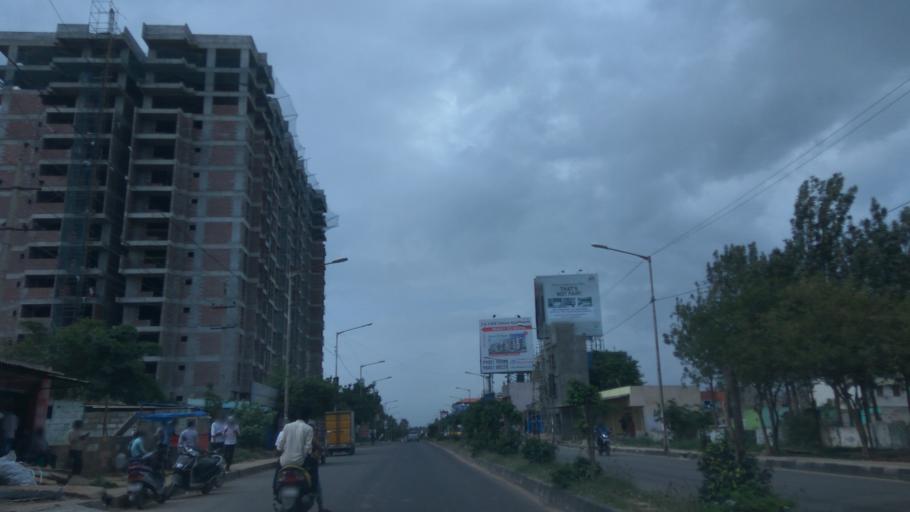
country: IN
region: Karnataka
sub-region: Bangalore Urban
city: Yelahanka
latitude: 13.0791
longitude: 77.6339
